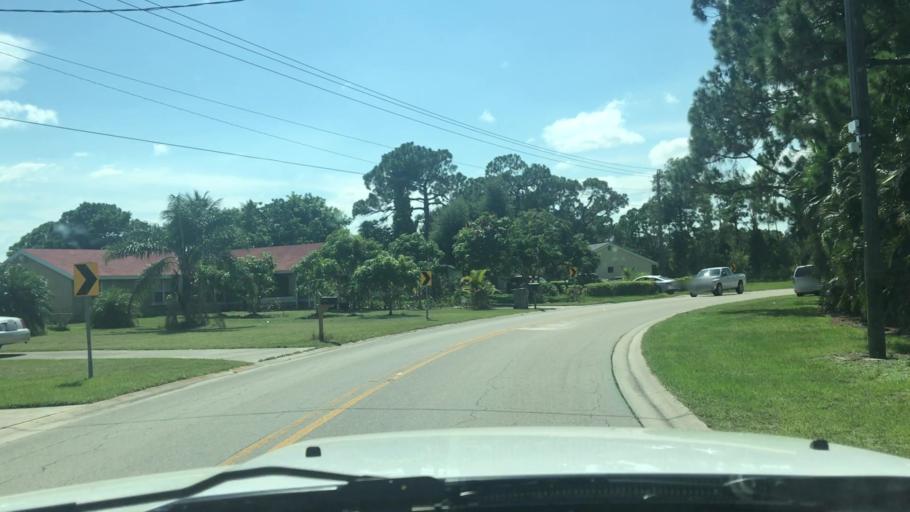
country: US
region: Florida
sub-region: Saint Lucie County
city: Lakewood Park
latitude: 27.5615
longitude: -80.3959
